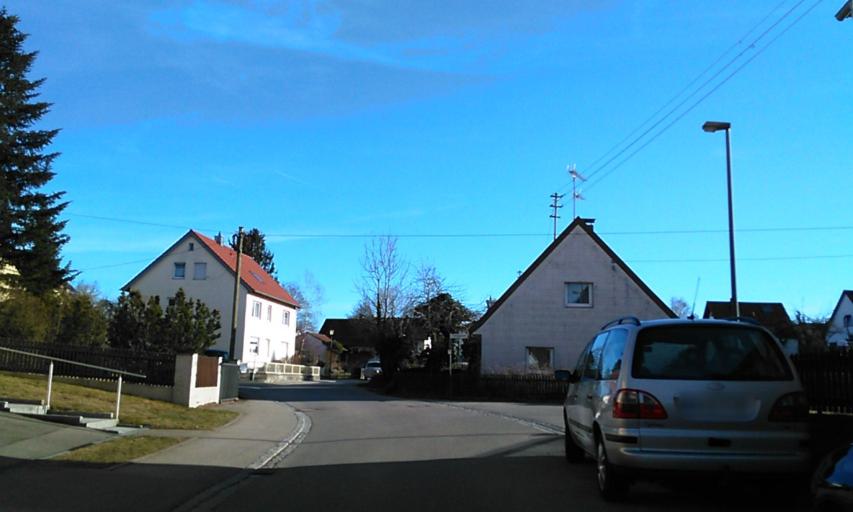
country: DE
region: Bavaria
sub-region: Swabia
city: Merching
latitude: 48.2430
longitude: 10.9837
